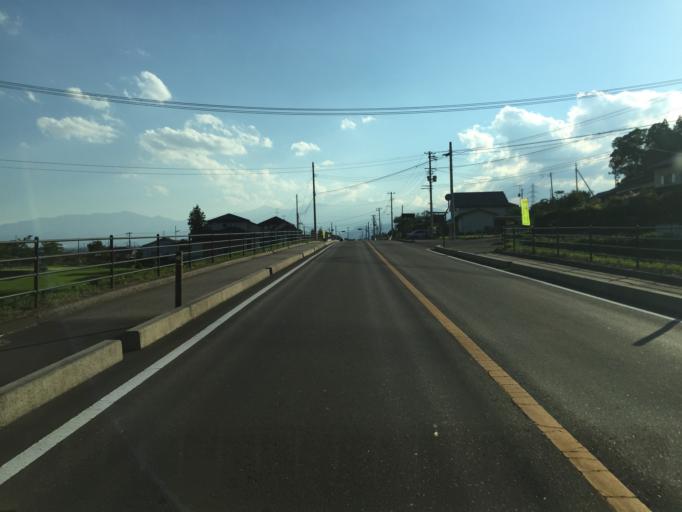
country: JP
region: Fukushima
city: Hobaramachi
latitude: 37.8333
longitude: 140.4870
